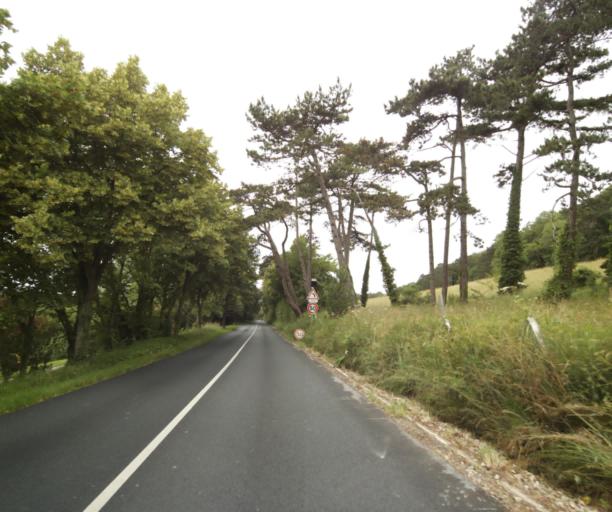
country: FR
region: Lower Normandy
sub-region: Departement du Calvados
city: Houlgate
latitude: 49.2866
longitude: -0.0848
